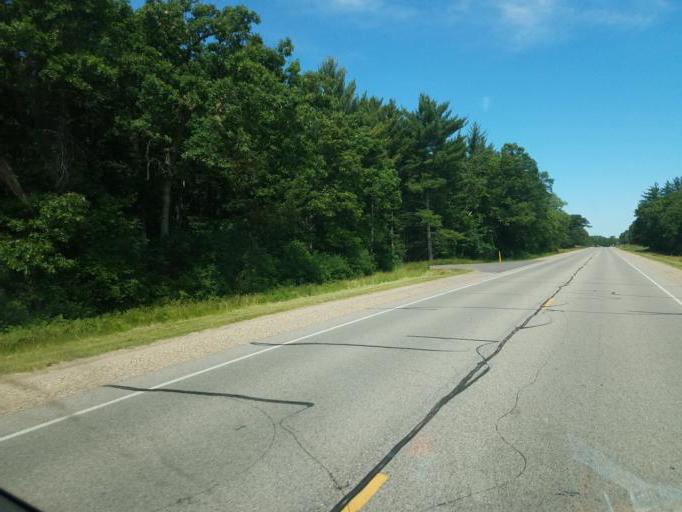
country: US
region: Wisconsin
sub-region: Columbia County
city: Wisconsin Dells
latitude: 43.6902
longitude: -89.8004
